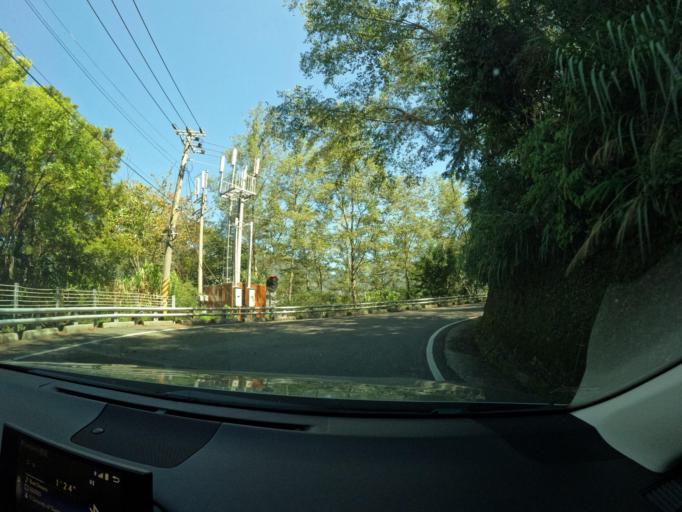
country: TW
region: Taiwan
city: Yujing
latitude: 23.2840
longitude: 120.8712
